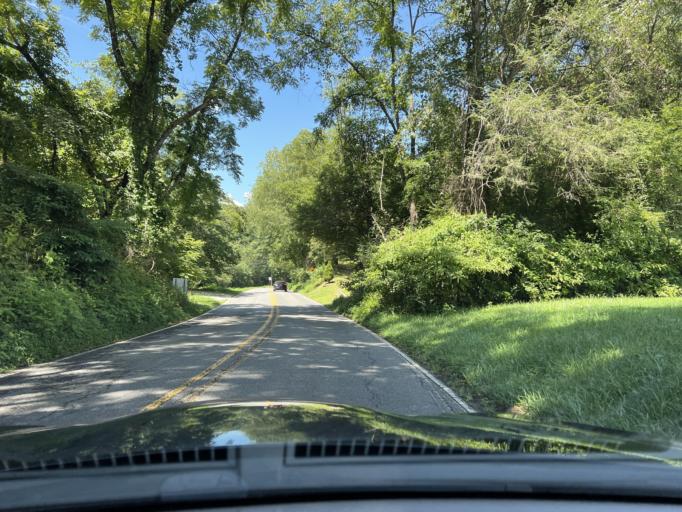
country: US
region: North Carolina
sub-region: Buncombe County
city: Fairview
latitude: 35.5166
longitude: -82.3988
